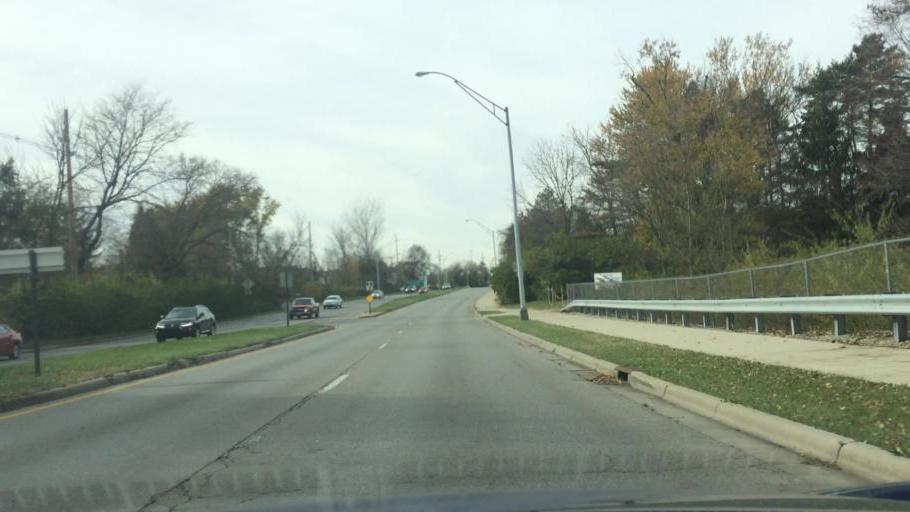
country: US
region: Ohio
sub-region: Franklin County
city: Worthington
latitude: 40.0522
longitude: -83.0389
